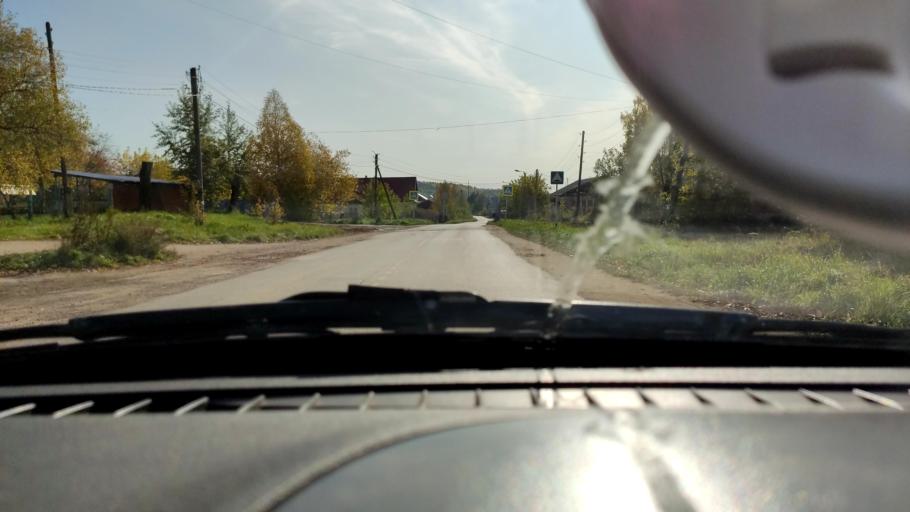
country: RU
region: Perm
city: Overyata
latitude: 58.0836
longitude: 55.8783
